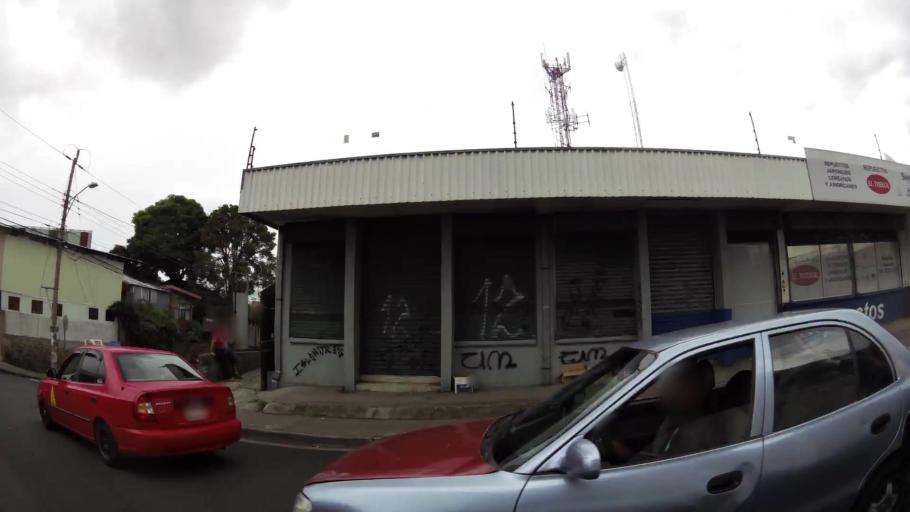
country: CR
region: San Jose
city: Colima
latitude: 9.9475
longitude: -84.0790
